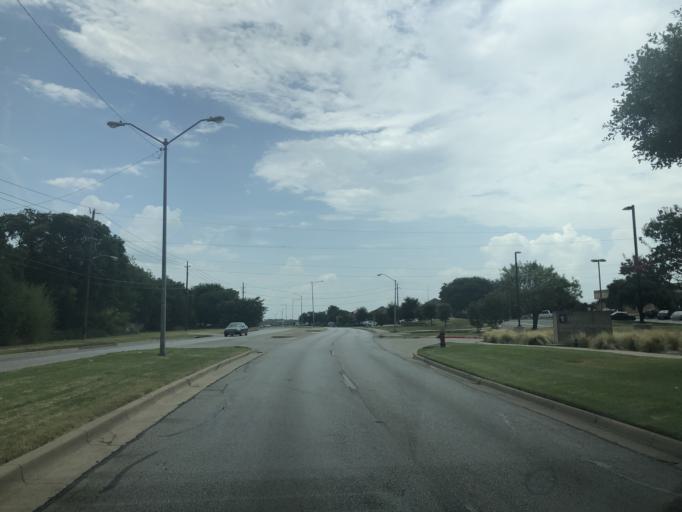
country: US
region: Texas
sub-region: Dallas County
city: Grand Prairie
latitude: 32.7375
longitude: -97.0144
